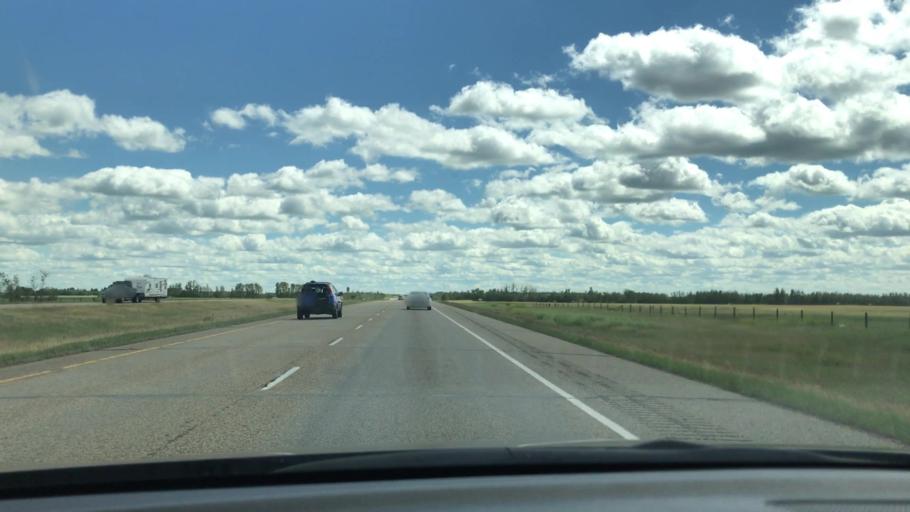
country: CA
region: Alberta
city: Leduc
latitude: 53.1556
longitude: -113.5984
